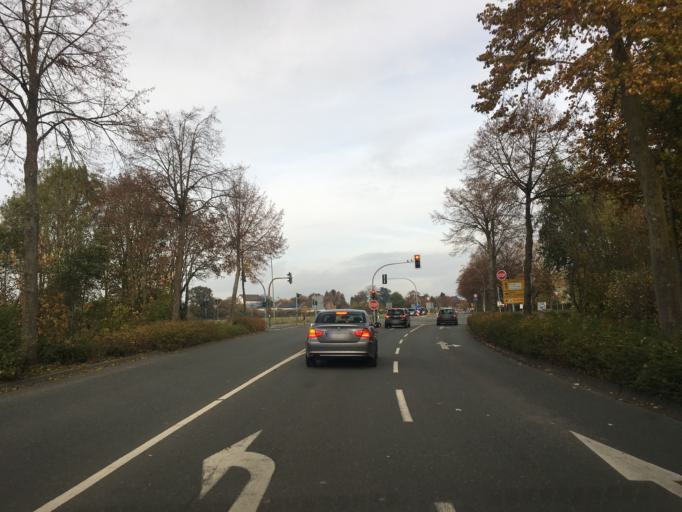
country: DE
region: North Rhine-Westphalia
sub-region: Regierungsbezirk Munster
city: Steinfurt
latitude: 52.1271
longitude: 7.3897
